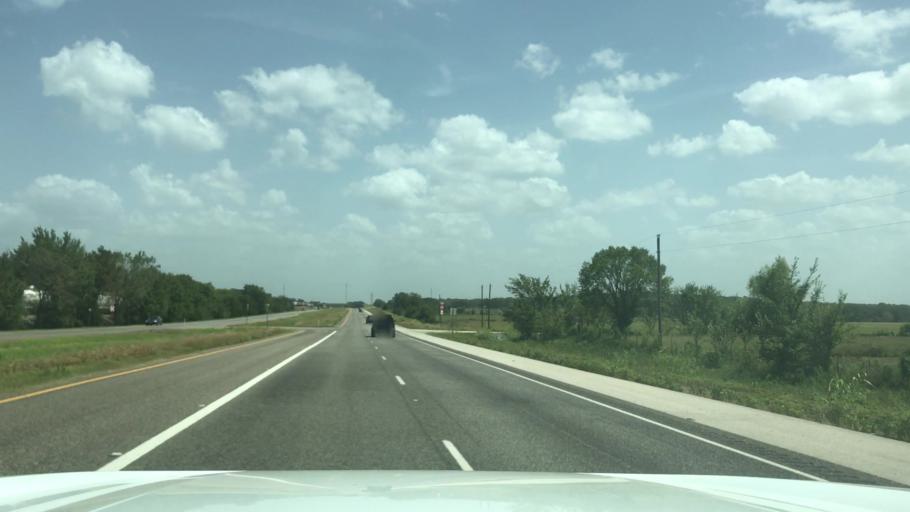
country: US
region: Texas
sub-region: Robertson County
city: Hearne
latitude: 30.9168
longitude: -96.6193
